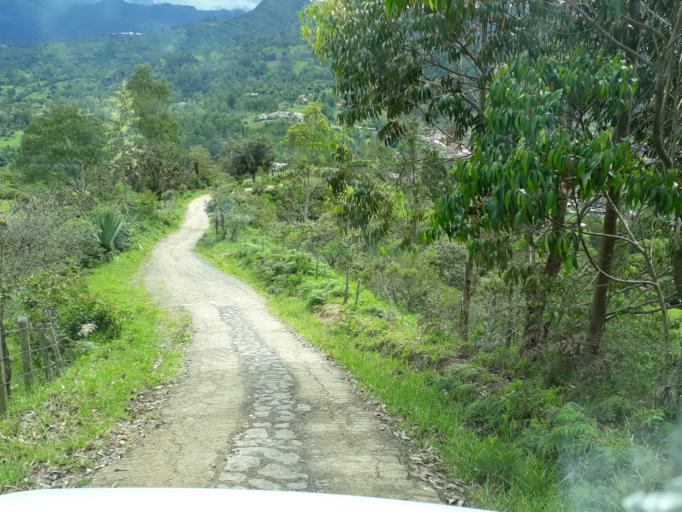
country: CO
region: Cundinamarca
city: Gacheta
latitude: 4.8103
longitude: -73.6437
